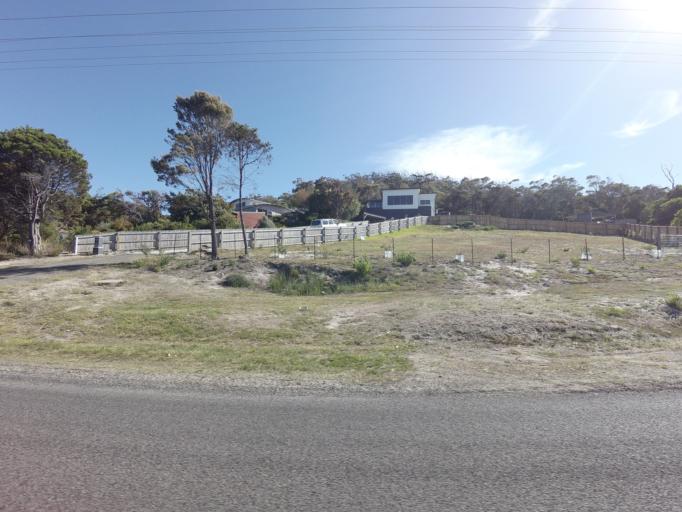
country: AU
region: Tasmania
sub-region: Break O'Day
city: St Helens
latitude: -41.8634
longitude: 148.2825
